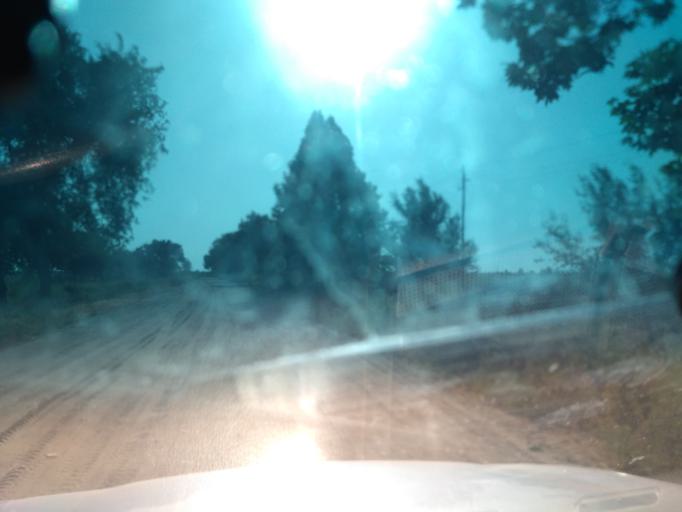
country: TJ
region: Viloyati Sughd
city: Buston
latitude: 40.5541
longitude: 69.0718
